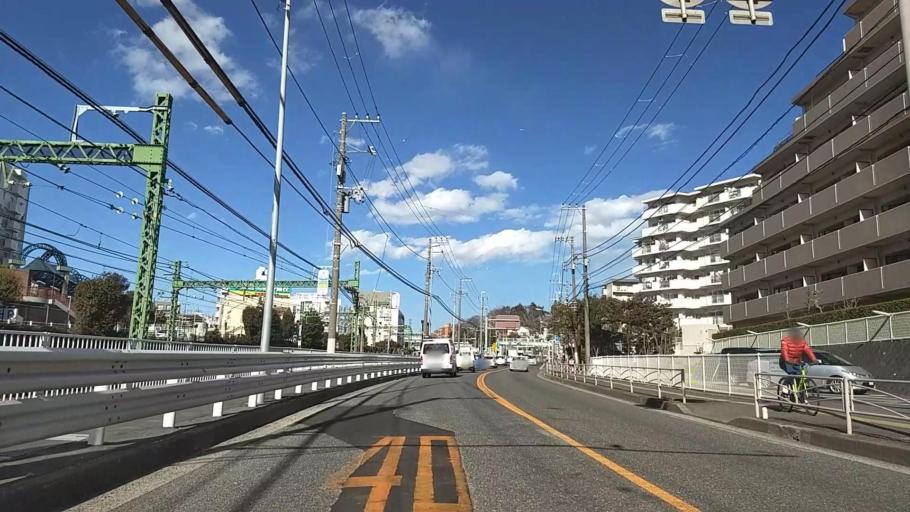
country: JP
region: Kanagawa
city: Zushi
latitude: 35.3582
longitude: 139.6283
